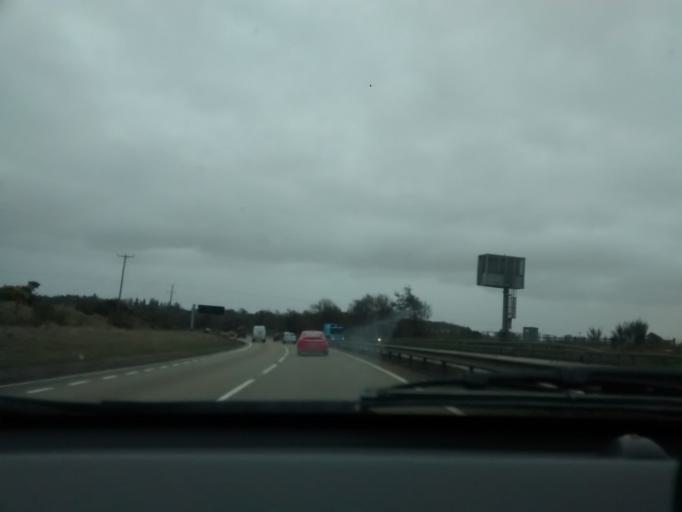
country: GB
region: England
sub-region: Suffolk
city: Kesgrave
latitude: 52.0242
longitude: 1.2288
